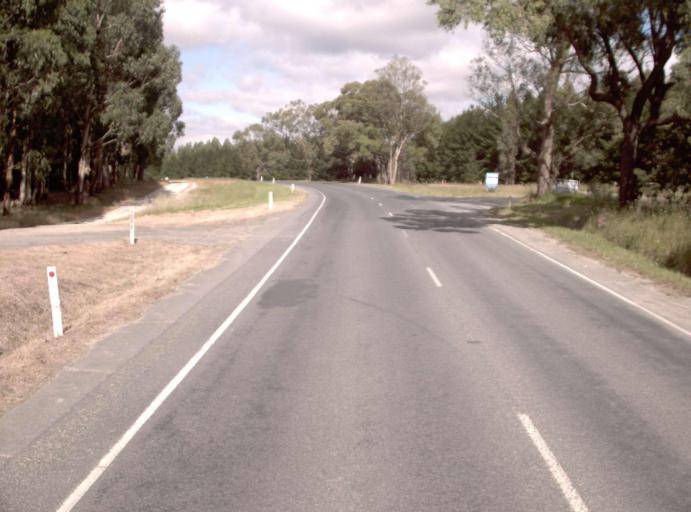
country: AU
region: Victoria
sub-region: Latrobe
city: Traralgon
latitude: -38.1861
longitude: 146.4760
